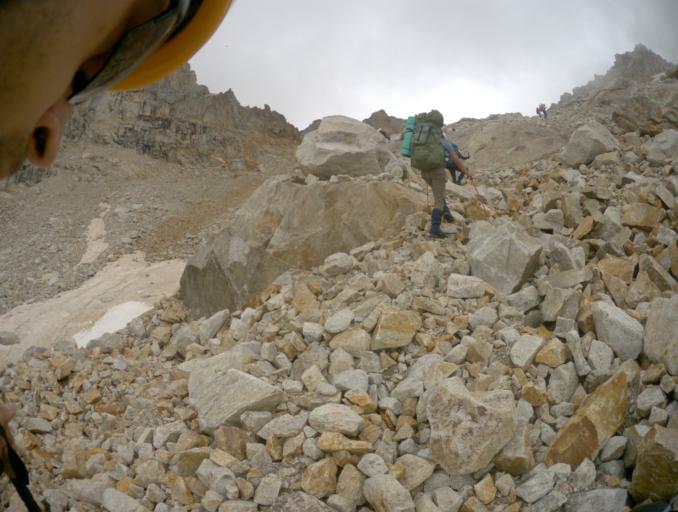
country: RU
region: Karachayevo-Cherkesiya
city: Uchkulan
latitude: 43.2796
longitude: 42.1124
